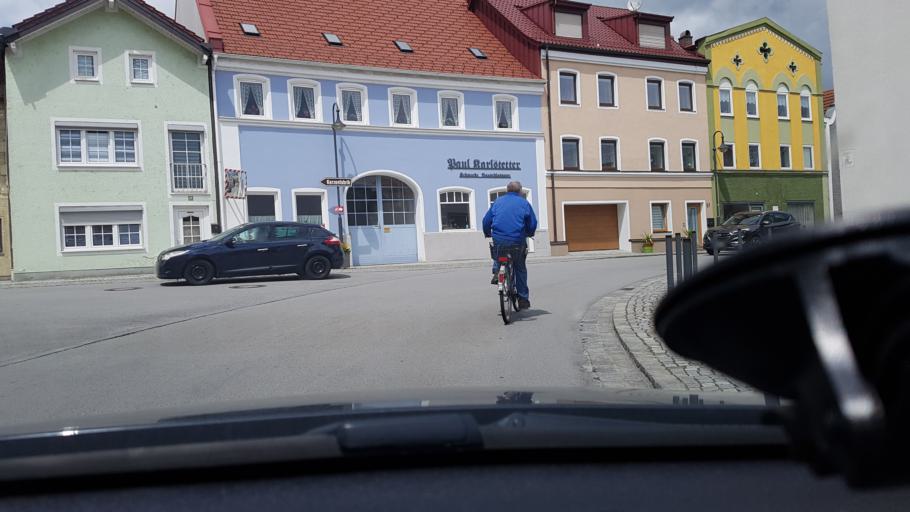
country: DE
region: Bavaria
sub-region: Lower Bavaria
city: Rotthalmunster
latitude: 48.3600
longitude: 13.2011
